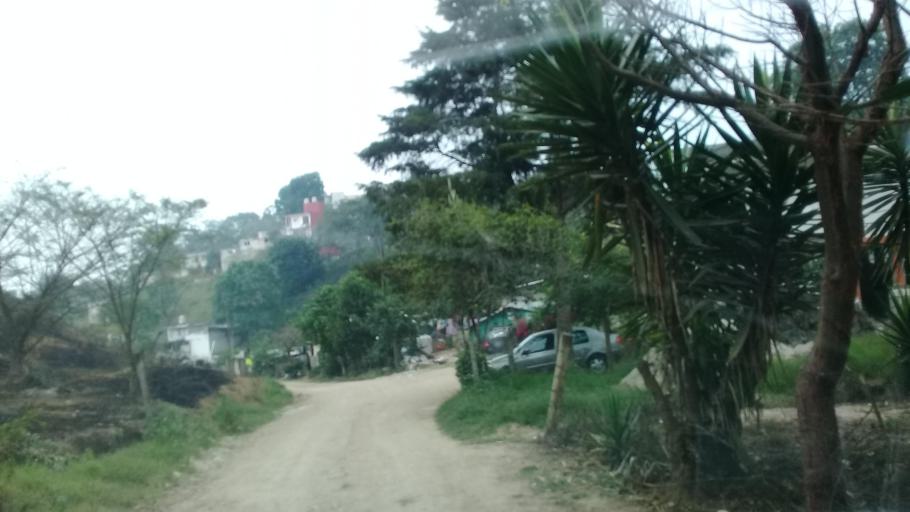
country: MX
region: Veracruz
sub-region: Xalapa
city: Fraccionamiento las Fuentes
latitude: 19.4944
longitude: -96.8981
